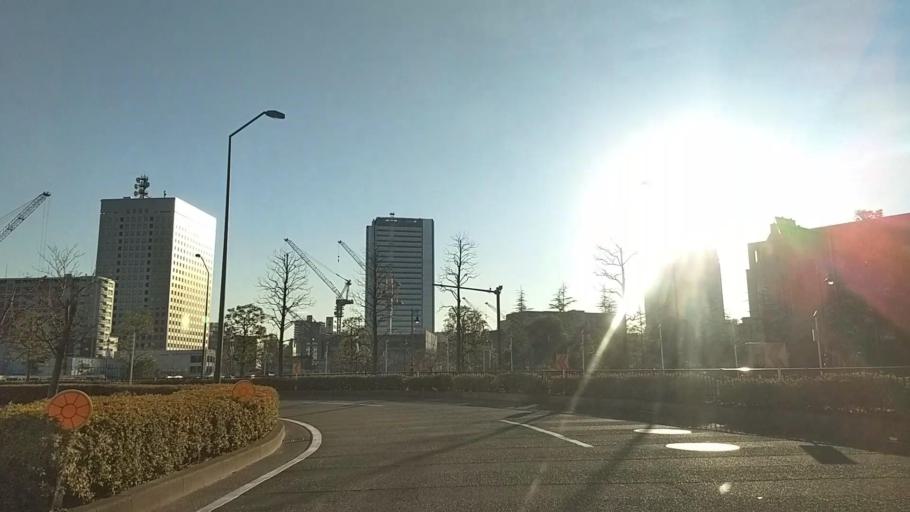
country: JP
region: Kanagawa
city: Yokohama
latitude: 35.4545
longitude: 139.6376
